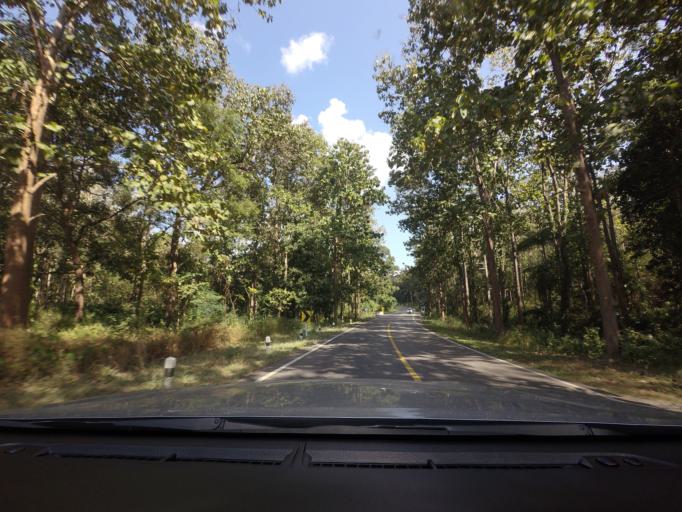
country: TH
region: Chiang Mai
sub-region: Amphoe Chiang Dao
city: Chiang Dao
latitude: 19.4721
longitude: 99.0034
